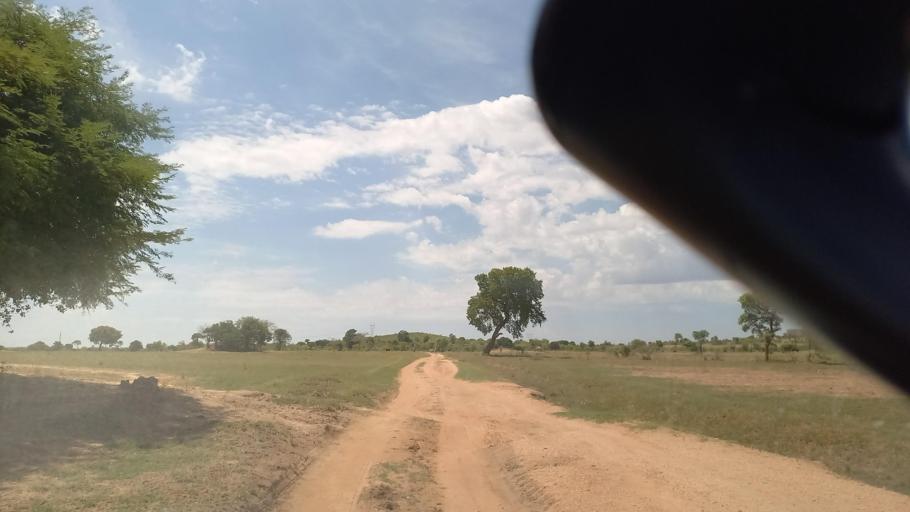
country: ZM
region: Southern
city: Mazabuka
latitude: -16.1521
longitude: 27.7795
